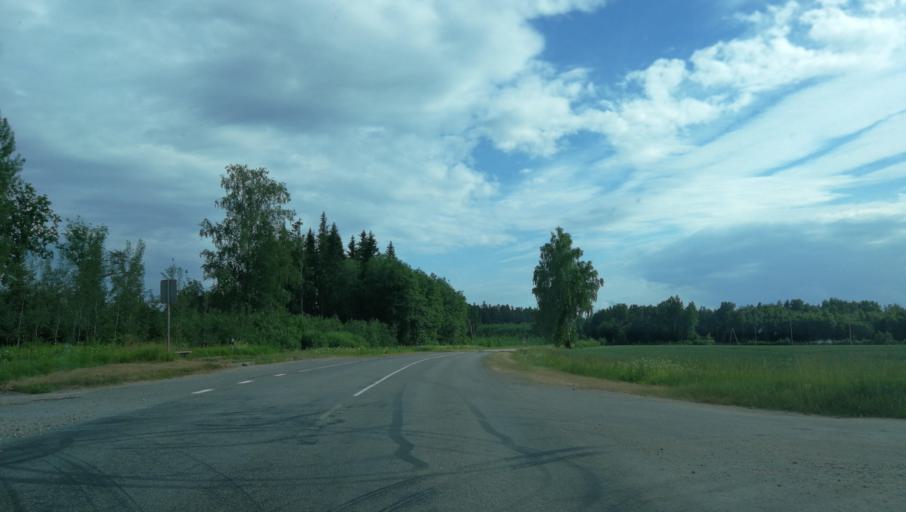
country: LV
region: Valmieras Rajons
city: Valmiera
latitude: 57.5880
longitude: 25.4613
